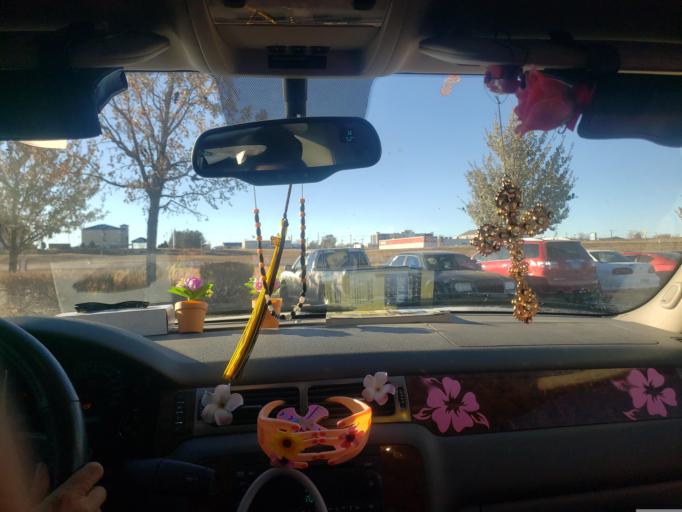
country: US
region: Kansas
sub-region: Finney County
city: Garden City
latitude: 37.9806
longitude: -100.8357
